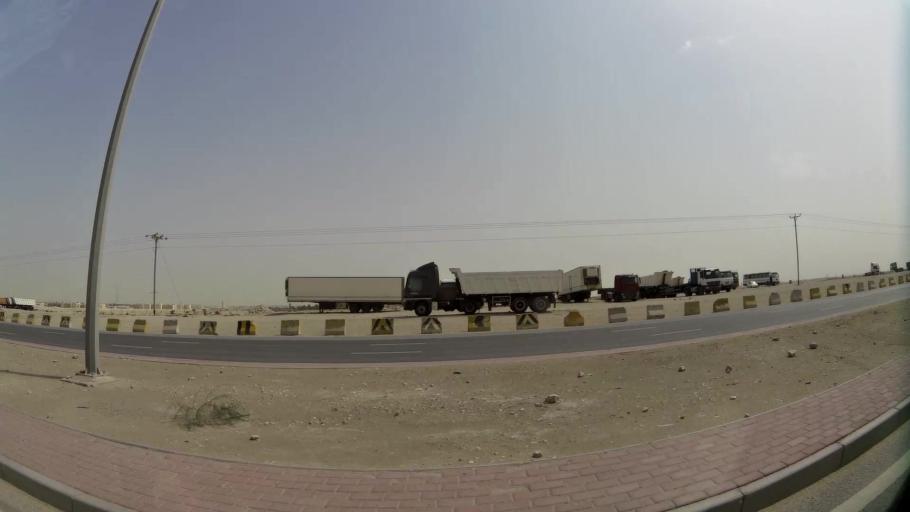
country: QA
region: Baladiyat ar Rayyan
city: Ar Rayyan
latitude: 25.2340
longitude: 51.3990
